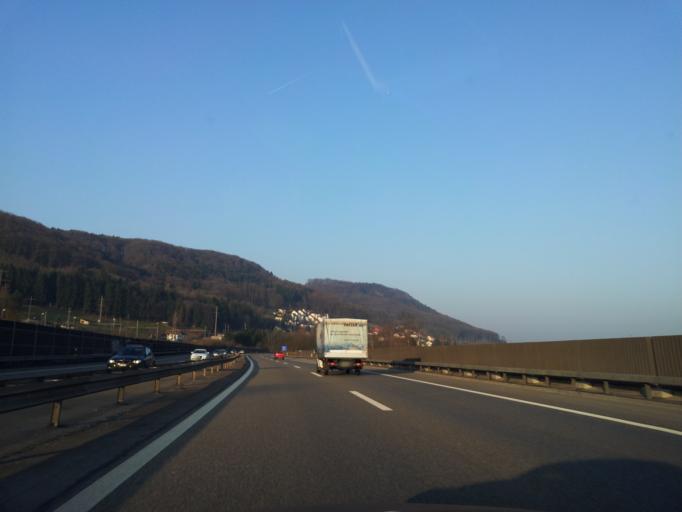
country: CH
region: Aargau
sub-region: Bezirk Rheinfelden
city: Stein
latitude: 47.5414
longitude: 7.9603
